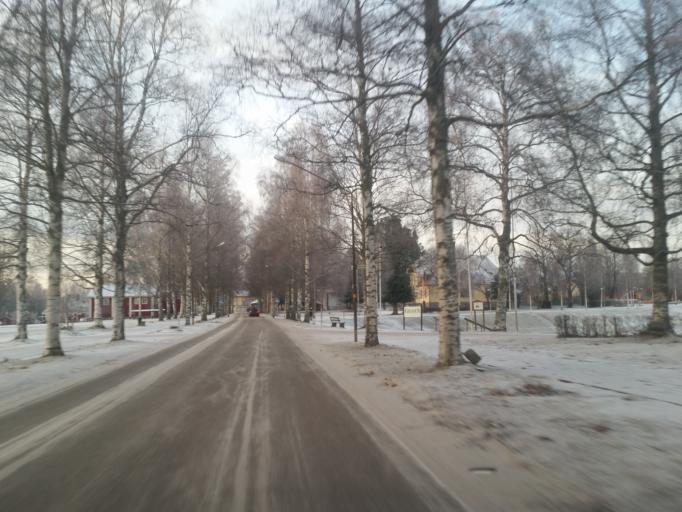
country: SE
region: Dalarna
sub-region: Leksand Municipality
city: Leksand
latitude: 60.7311
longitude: 14.9921
